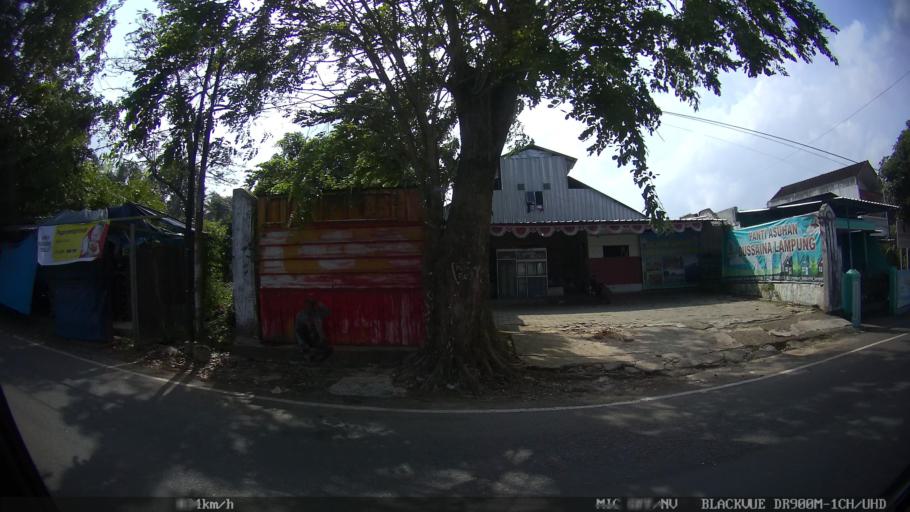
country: ID
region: Lampung
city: Kedaton
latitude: -5.3702
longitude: 105.2550
